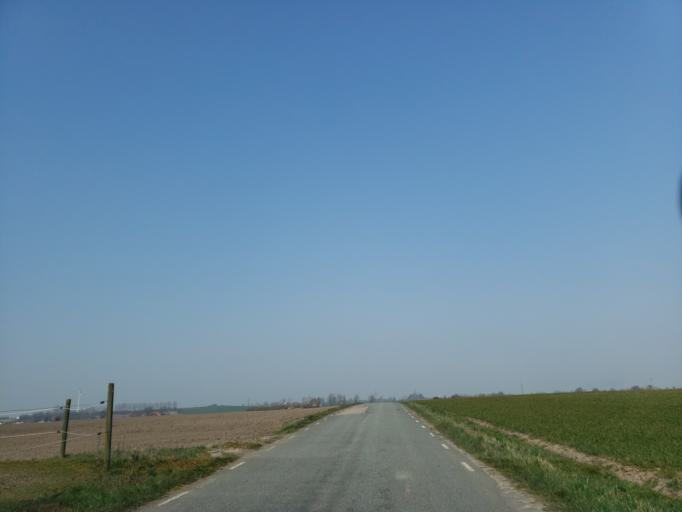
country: SE
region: Skane
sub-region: Simrishamns Kommun
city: Simrishamn
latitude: 55.4581
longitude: 14.2128
